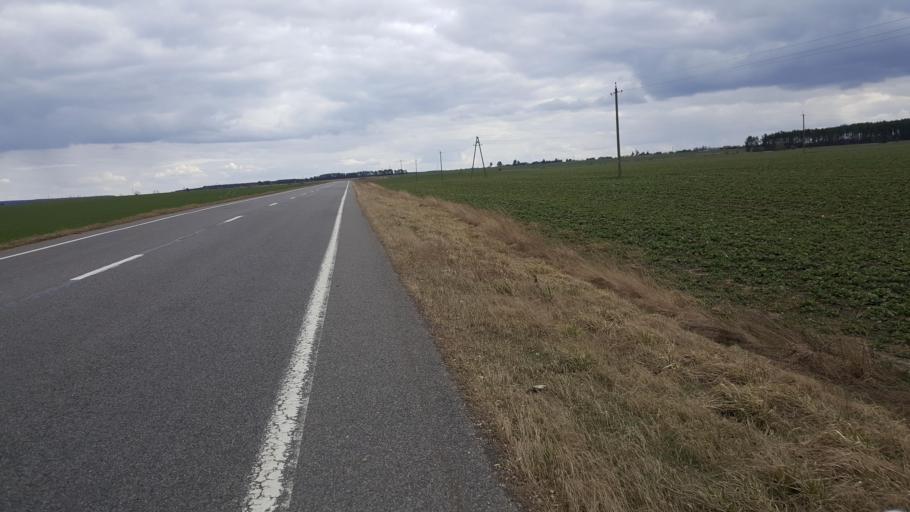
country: BY
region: Brest
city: Kamyanyets
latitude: 52.4182
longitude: 23.8459
